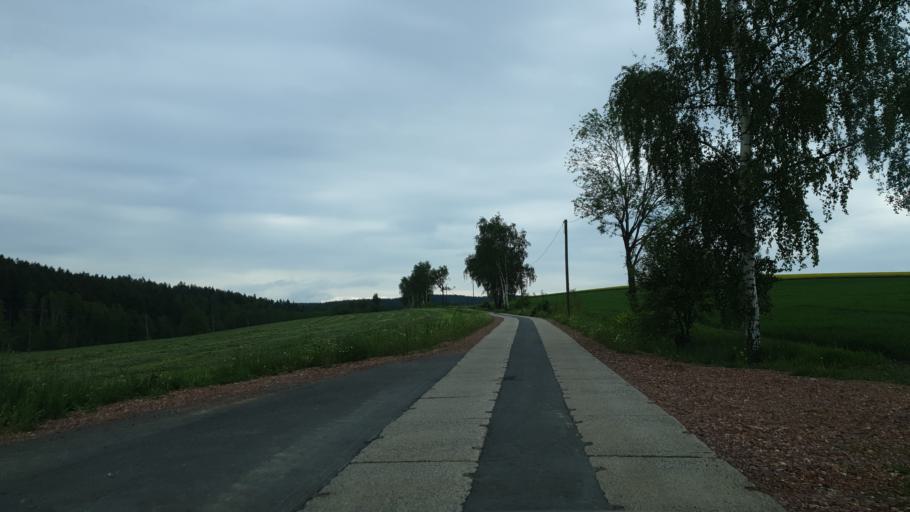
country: DE
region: Saxony
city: Stollberg
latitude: 50.6954
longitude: 12.7794
